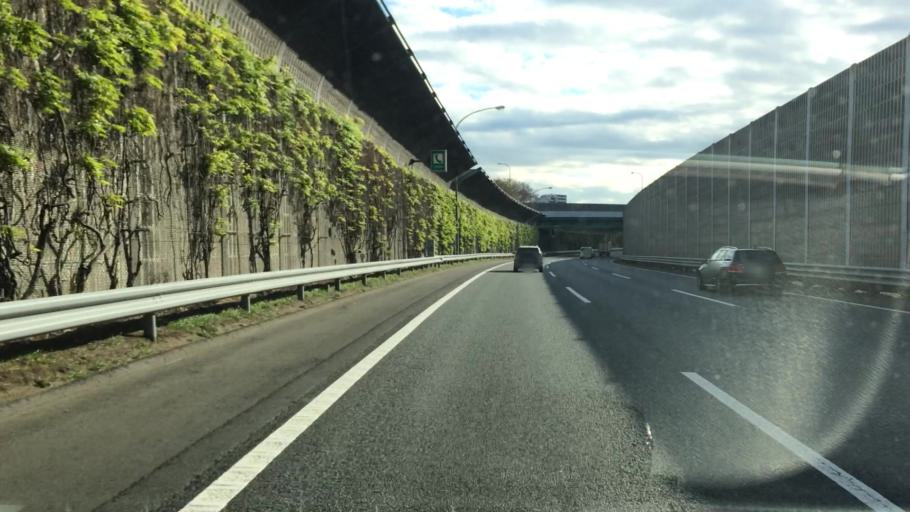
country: JP
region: Chiba
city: Chiba
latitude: 35.6489
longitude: 140.0612
